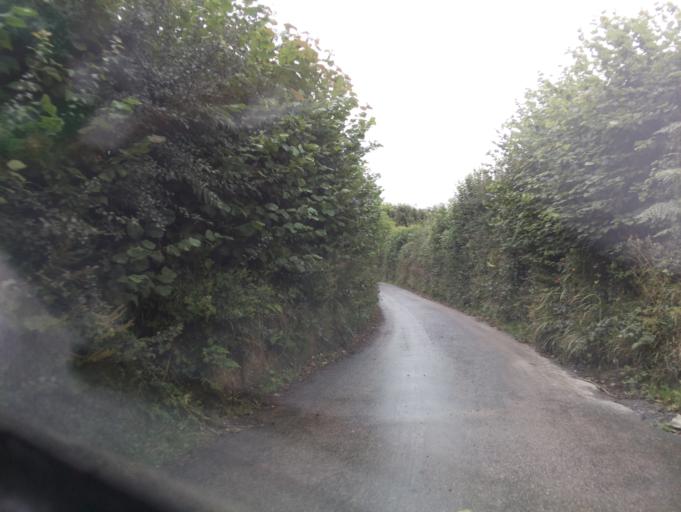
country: GB
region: England
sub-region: Devon
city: Totnes
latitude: 50.3440
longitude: -3.6839
